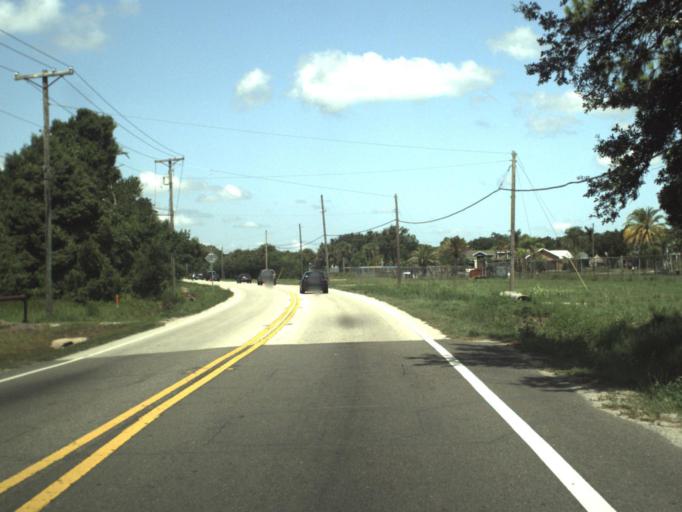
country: US
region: Florida
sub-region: Orange County
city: Conway
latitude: 28.4806
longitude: -81.2904
